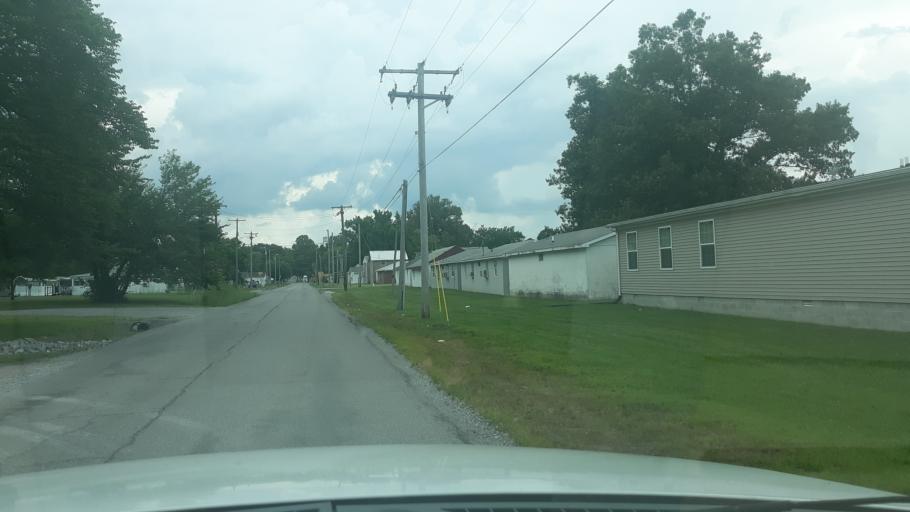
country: US
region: Illinois
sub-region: Saline County
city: Eldorado
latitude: 37.8041
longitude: -88.4566
